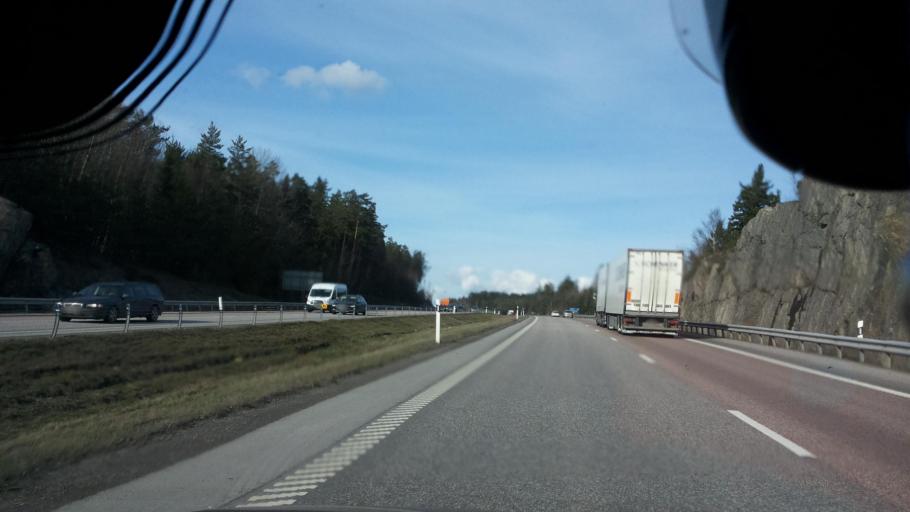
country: SE
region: Soedermanland
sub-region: Trosa Kommun
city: Vagnharad
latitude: 59.0186
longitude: 17.5516
